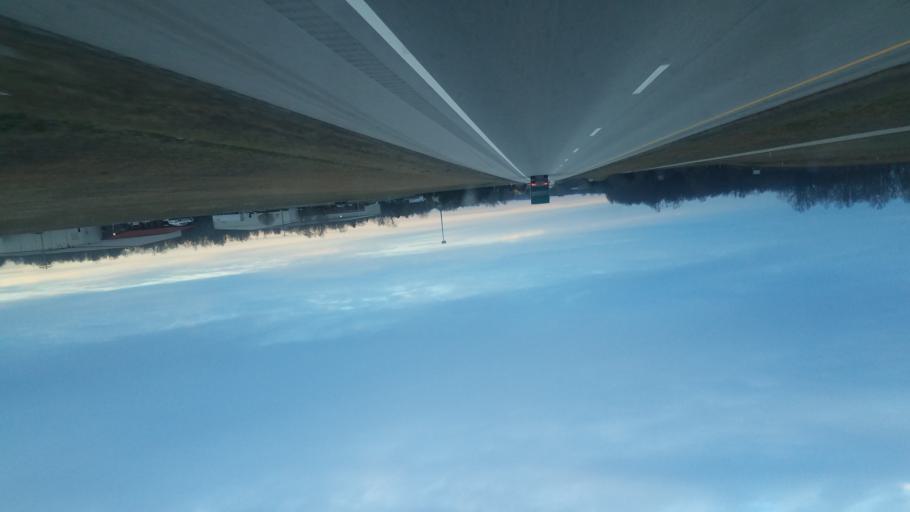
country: US
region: Tennessee
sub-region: Putnam County
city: Cookeville
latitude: 36.0559
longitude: -85.5073
